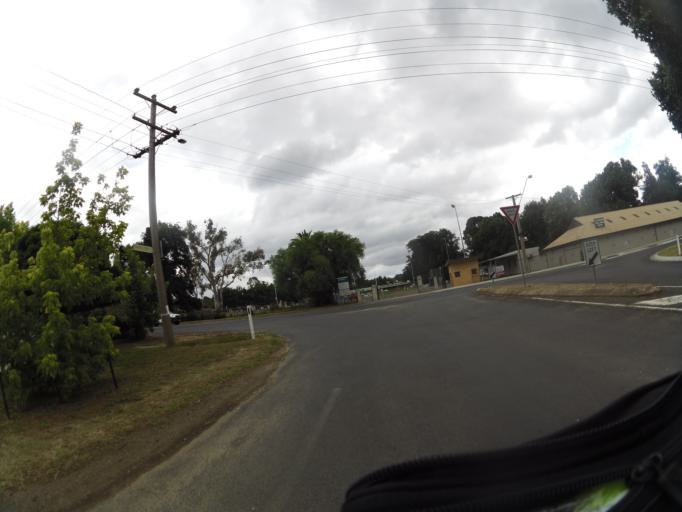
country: AU
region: Victoria
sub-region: Mount Alexander
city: Castlemaine
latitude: -37.0665
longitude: 144.2124
